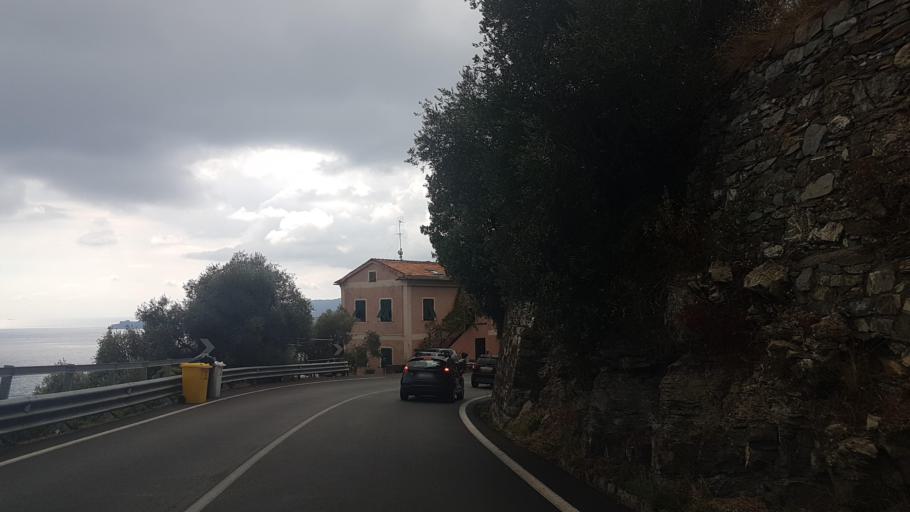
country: IT
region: Liguria
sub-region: Provincia di Genova
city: Zoagli
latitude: 44.3322
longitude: 9.2832
